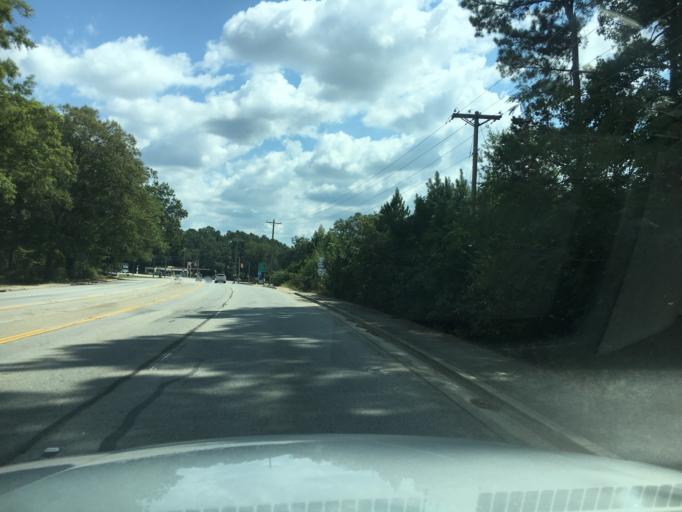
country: US
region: South Carolina
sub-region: Greenwood County
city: Greenwood
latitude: 34.1958
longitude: -82.1913
